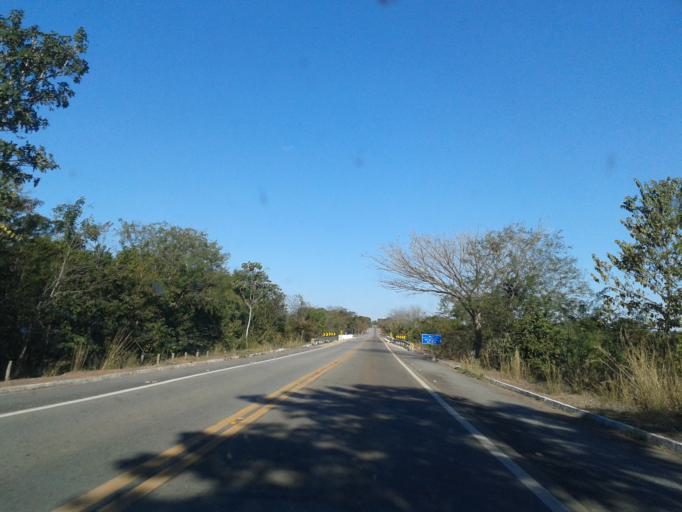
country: BR
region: Goias
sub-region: Mozarlandia
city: Mozarlandia
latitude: -15.1379
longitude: -50.5912
